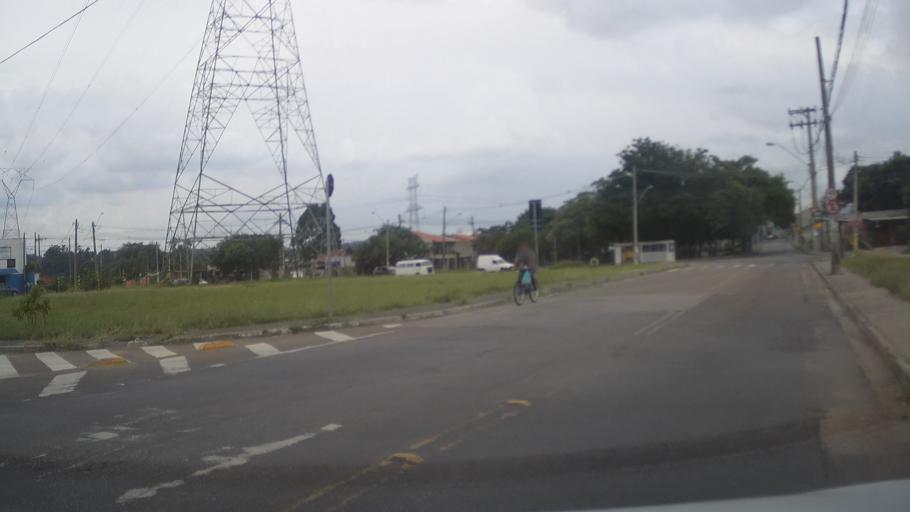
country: BR
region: Sao Paulo
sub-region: Itupeva
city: Itupeva
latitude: -23.1440
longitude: -46.9973
